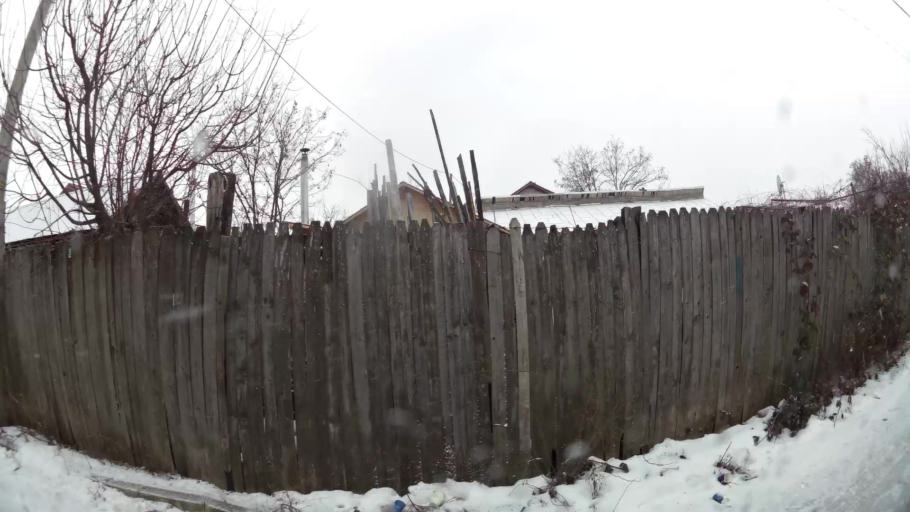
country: RO
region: Dambovita
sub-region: Municipiul Targoviste
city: Targoviste
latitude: 44.9300
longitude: 25.4321
